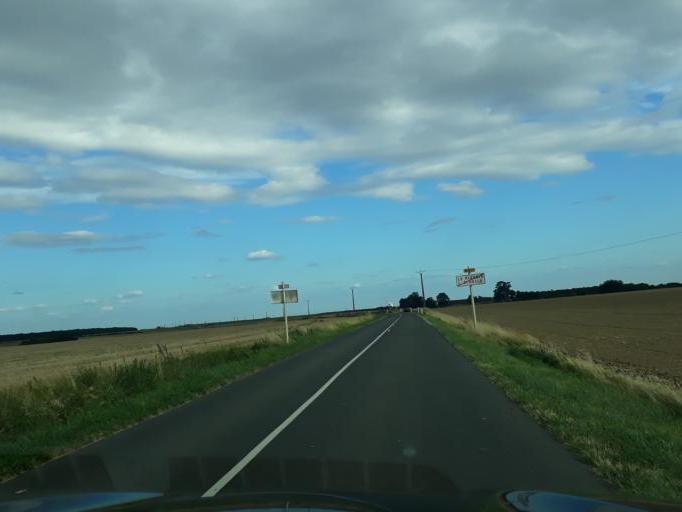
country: FR
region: Centre
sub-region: Departement du Loir-et-Cher
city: Mer
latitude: 47.8126
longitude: 1.4292
